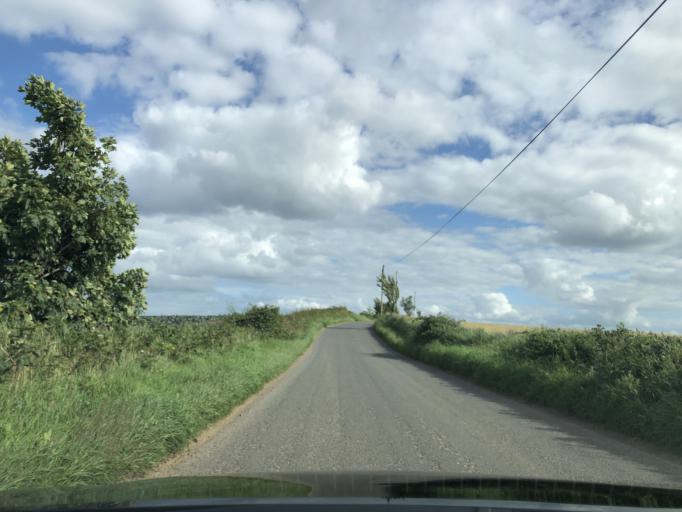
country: GB
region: Northern Ireland
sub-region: Ards District
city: Newtownards
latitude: 54.5639
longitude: -5.7109
